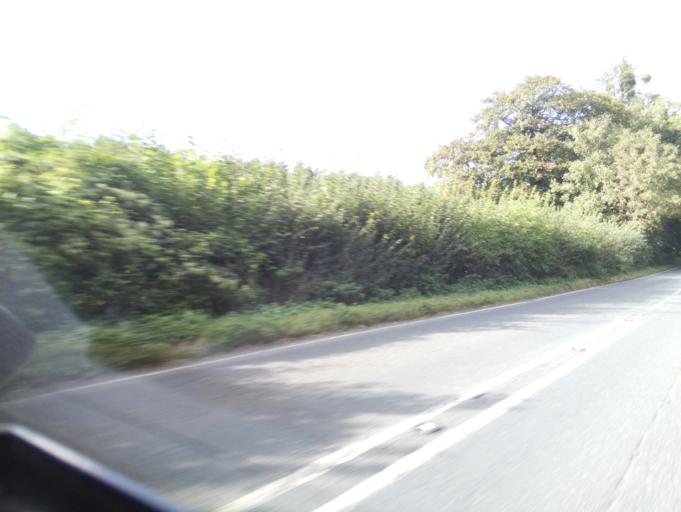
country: GB
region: England
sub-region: Hampshire
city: Basingstoke
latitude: 51.2429
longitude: -1.0784
